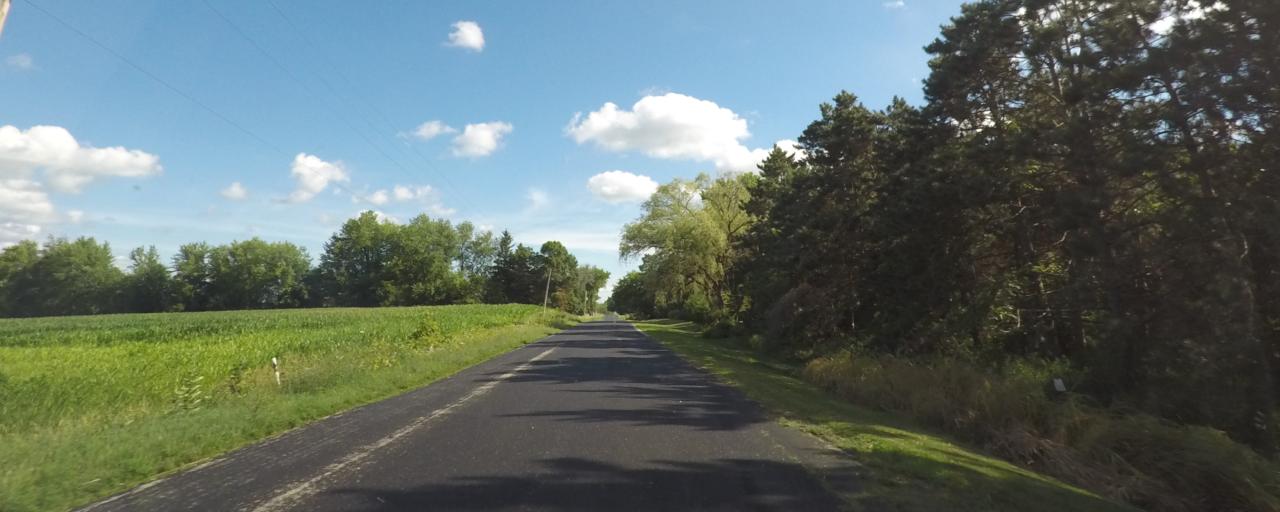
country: US
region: Wisconsin
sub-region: Rock County
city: Edgerton
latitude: 42.8522
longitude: -89.1320
